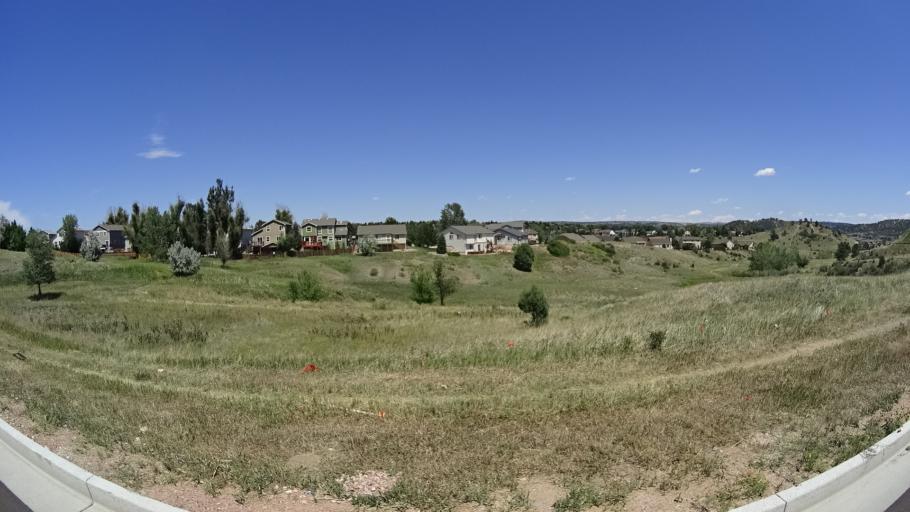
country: US
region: Colorado
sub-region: El Paso County
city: Air Force Academy
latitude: 38.9182
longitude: -104.8357
